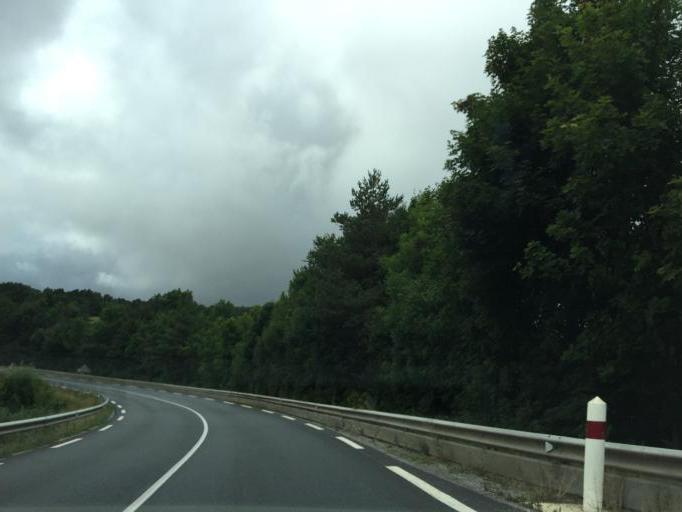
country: FR
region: Midi-Pyrenees
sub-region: Departement de l'Aveyron
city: Severac-le-Chateau
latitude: 44.2370
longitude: 2.9854
